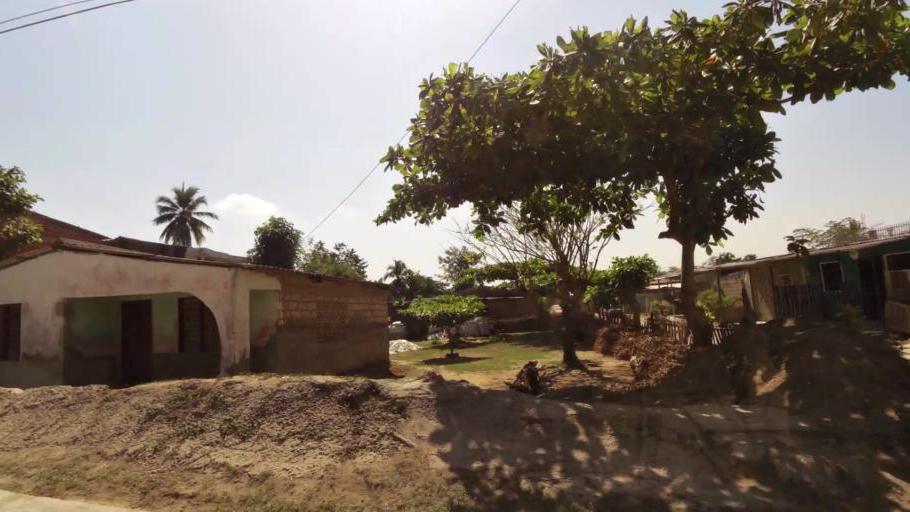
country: CO
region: Bolivar
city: Cartagena
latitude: 10.3578
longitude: -75.4903
